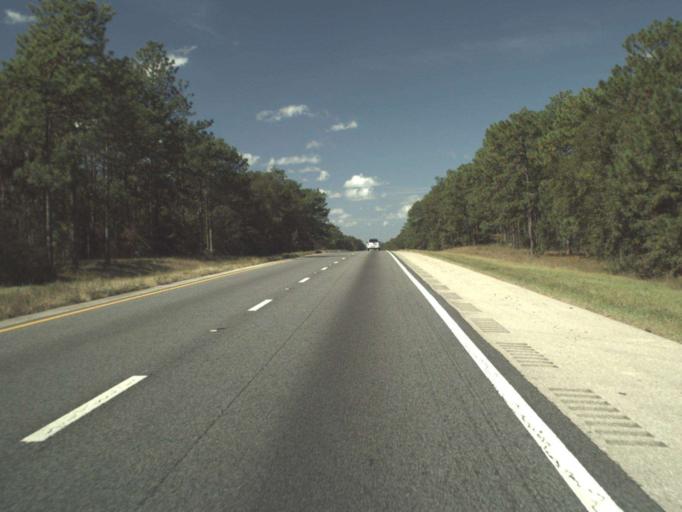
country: US
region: Florida
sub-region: Washington County
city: Chipley
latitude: 30.7460
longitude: -85.4863
